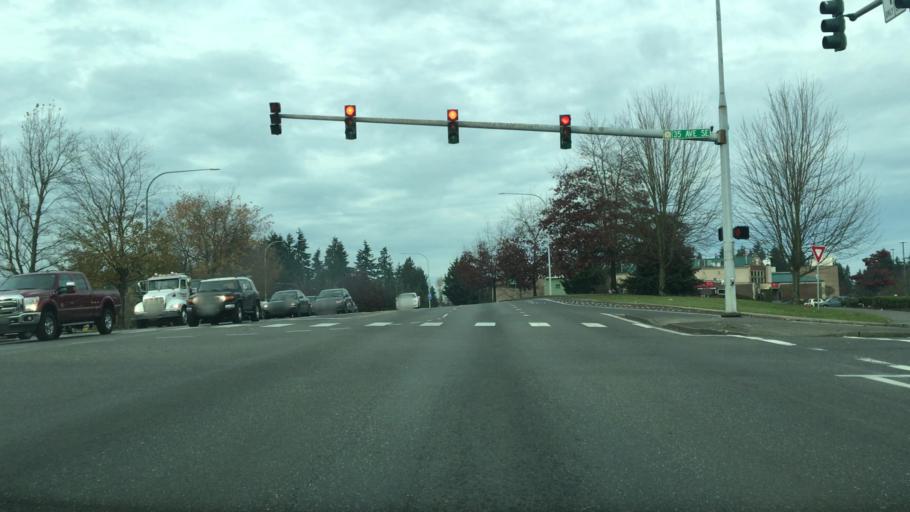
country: US
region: Washington
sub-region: Pierce County
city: Puyallup
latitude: 47.1585
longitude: -122.2930
